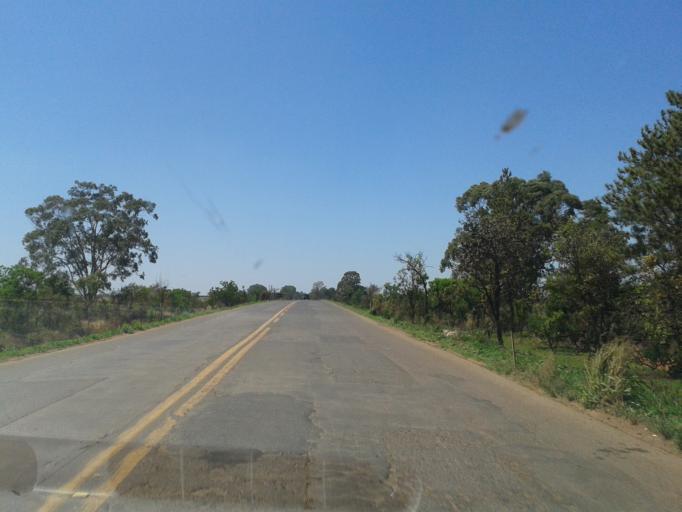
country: BR
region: Minas Gerais
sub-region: Araxa
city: Araxa
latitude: -19.4020
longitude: -47.3190
